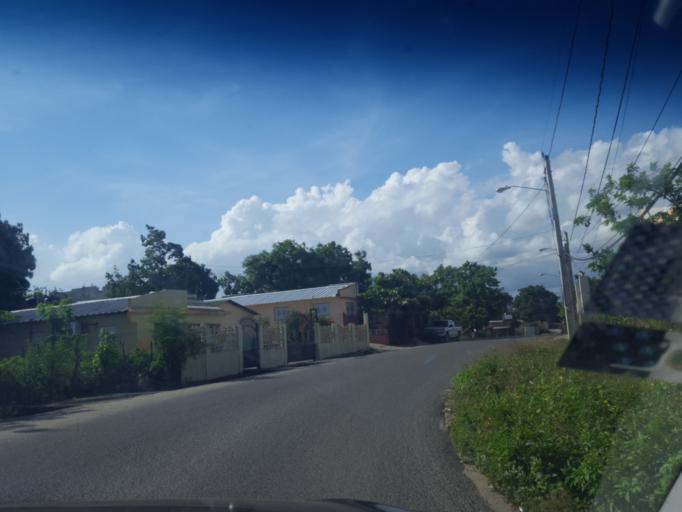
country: DO
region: La Vega
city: Rio Verde Arriba
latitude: 19.3601
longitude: -70.6055
